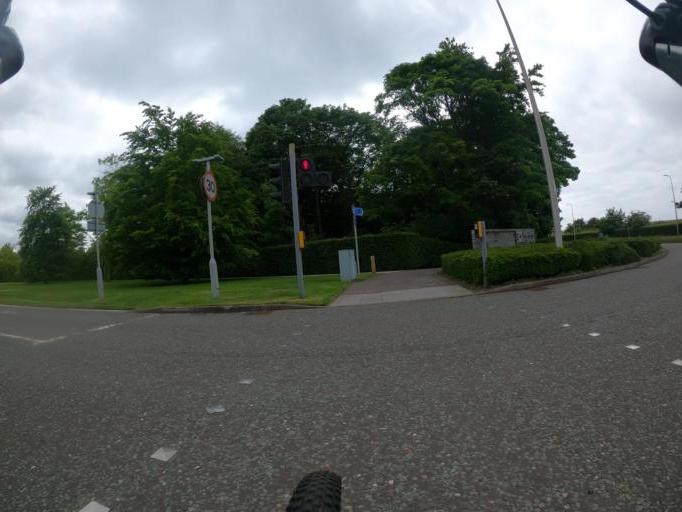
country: GB
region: Scotland
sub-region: Edinburgh
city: Ratho
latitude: 55.9365
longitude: -3.3360
